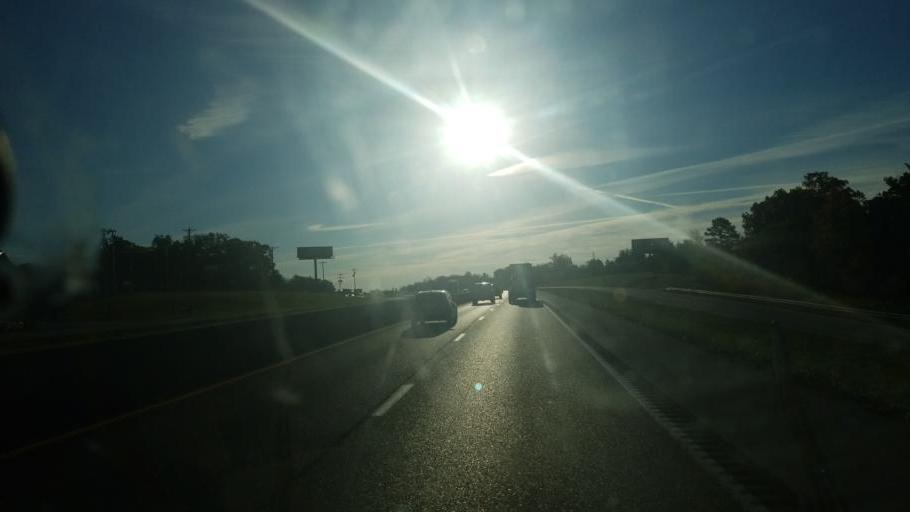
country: US
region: Missouri
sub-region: Warren County
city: Wright City
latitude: 38.8286
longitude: -91.0116
